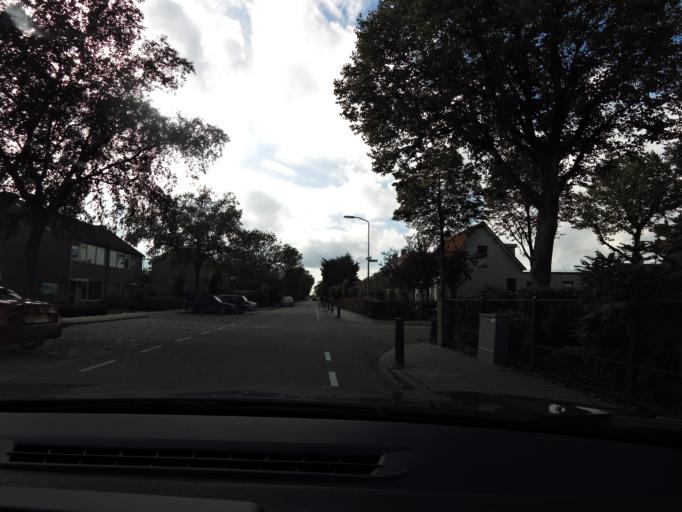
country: NL
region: South Holland
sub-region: Gemeente Goeree-Overflakkee
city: Dirksland
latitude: 51.7457
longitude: 4.0945
